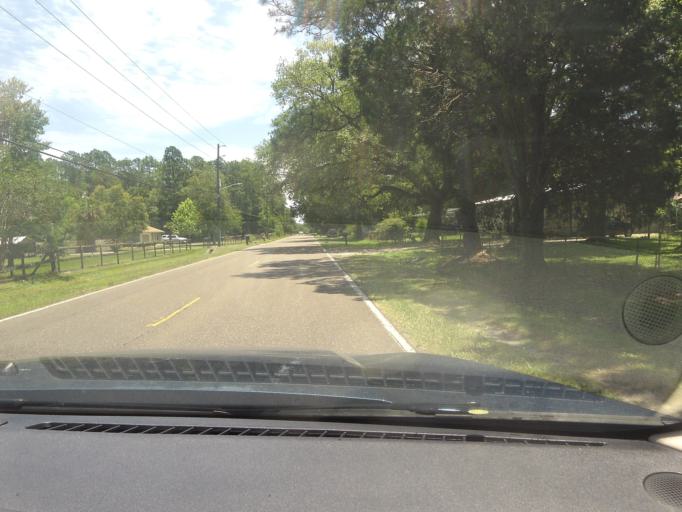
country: US
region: Florida
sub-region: Duval County
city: Jacksonville
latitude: 30.4617
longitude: -81.5404
